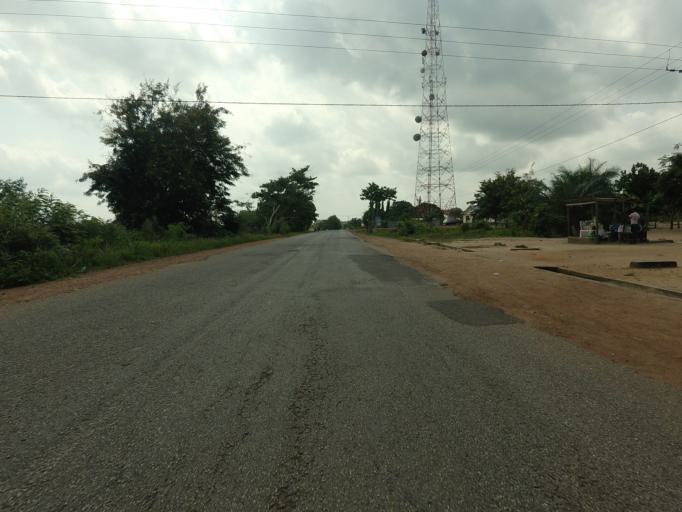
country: GH
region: Volta
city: Ho
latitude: 6.4201
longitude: 0.7387
